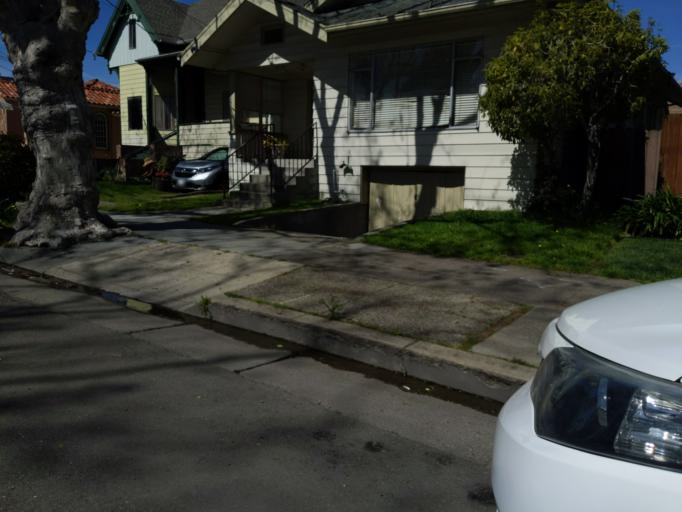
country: US
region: California
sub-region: Alameda County
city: Alameda
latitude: 37.7620
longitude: -122.2378
